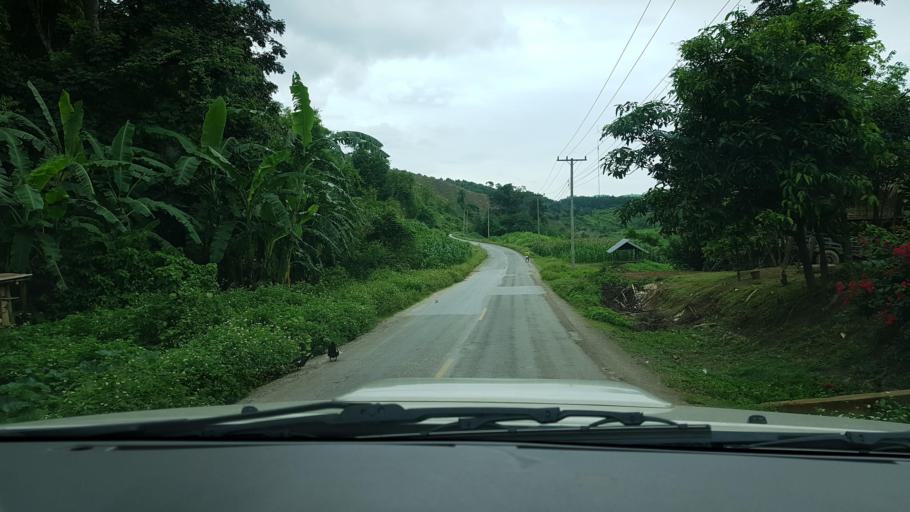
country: LA
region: Loungnamtha
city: Muang Nale
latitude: 20.2173
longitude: 101.5454
